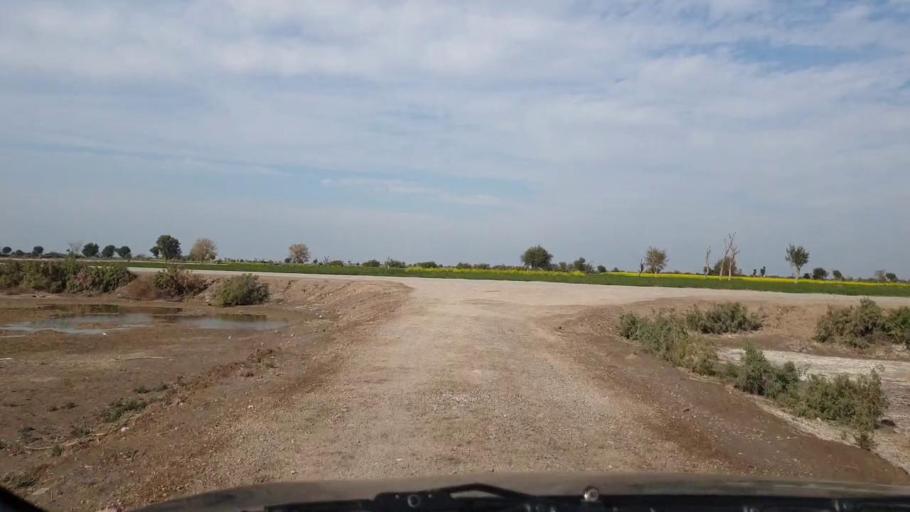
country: PK
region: Sindh
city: Sinjhoro
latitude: 26.0302
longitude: 68.8206
